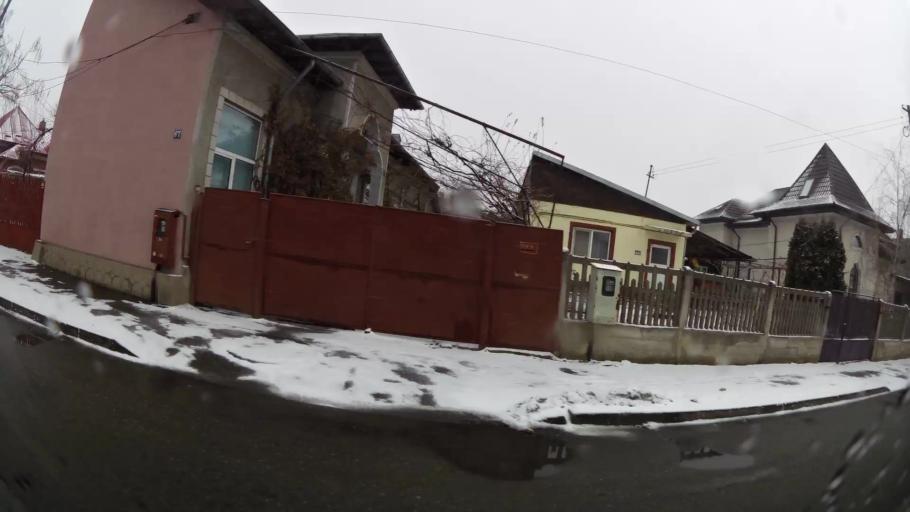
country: RO
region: Dambovita
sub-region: Municipiul Targoviste
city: Targoviste
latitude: 44.9381
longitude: 25.4473
